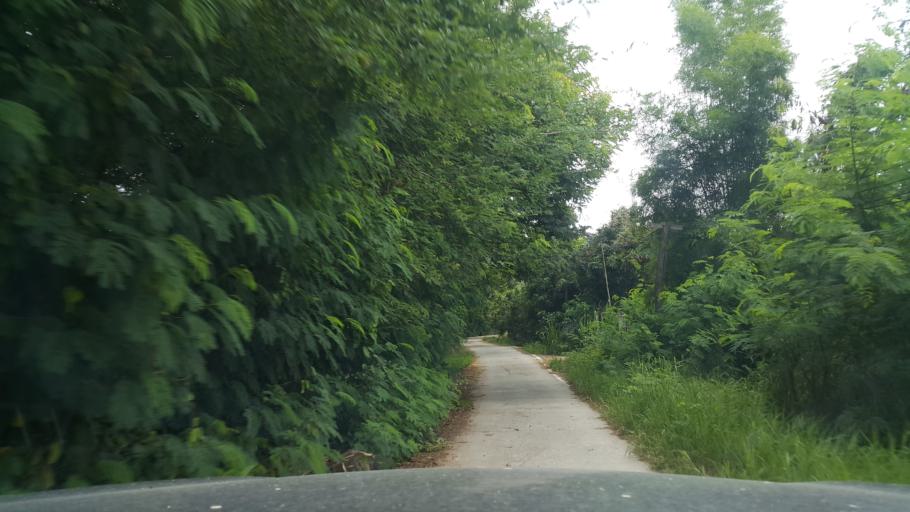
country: TH
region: Lamphun
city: Ban Thi
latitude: 18.6718
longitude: 99.1474
